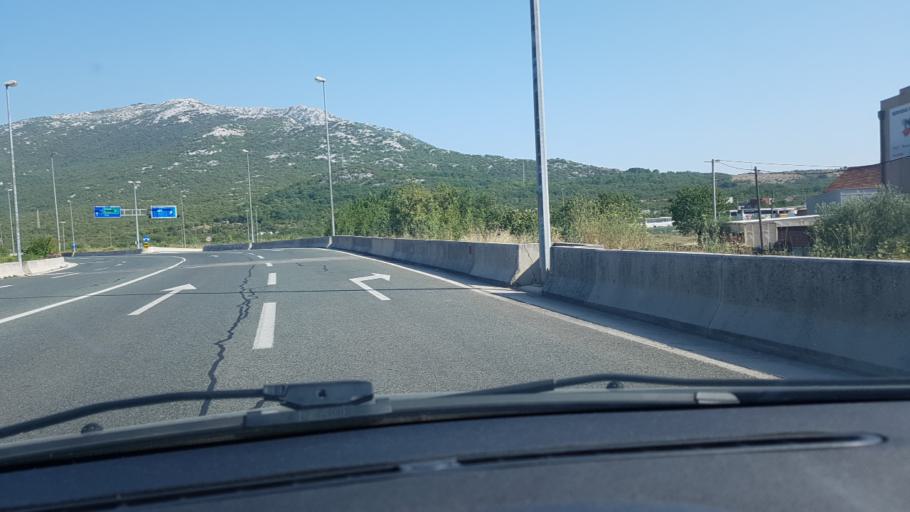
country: HR
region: Splitsko-Dalmatinska
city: Klis
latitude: 43.5768
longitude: 16.5366
